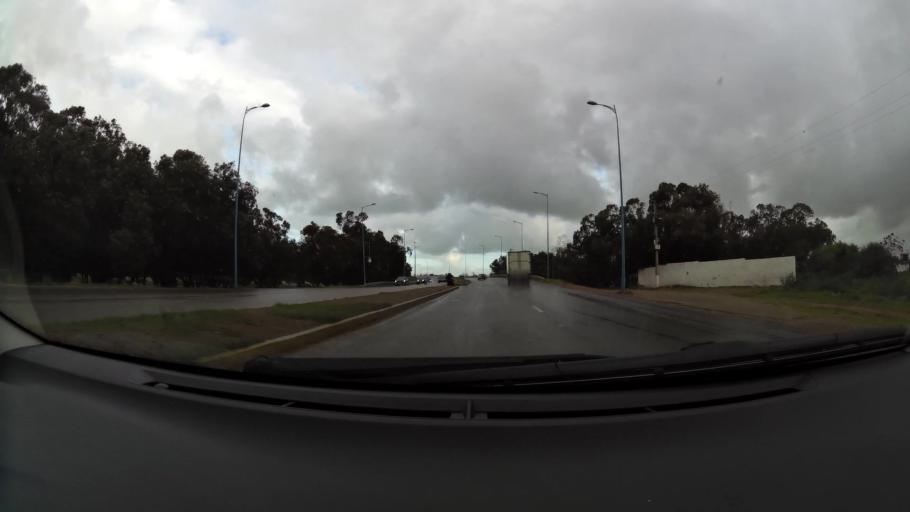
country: MA
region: Grand Casablanca
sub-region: Mohammedia
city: Mohammedia
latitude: 33.6717
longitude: -7.4069
